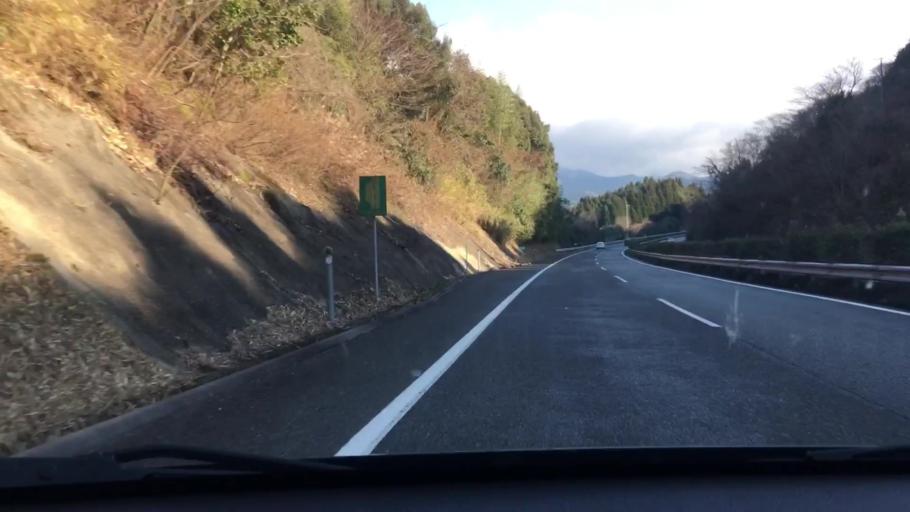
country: JP
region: Kumamoto
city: Hitoyoshi
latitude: 32.1797
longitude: 130.7855
